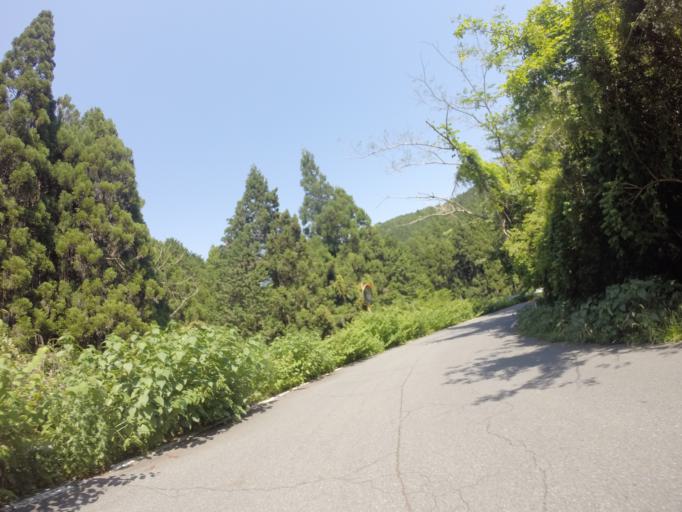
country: JP
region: Shizuoka
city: Fujinomiya
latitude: 35.1607
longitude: 138.5710
